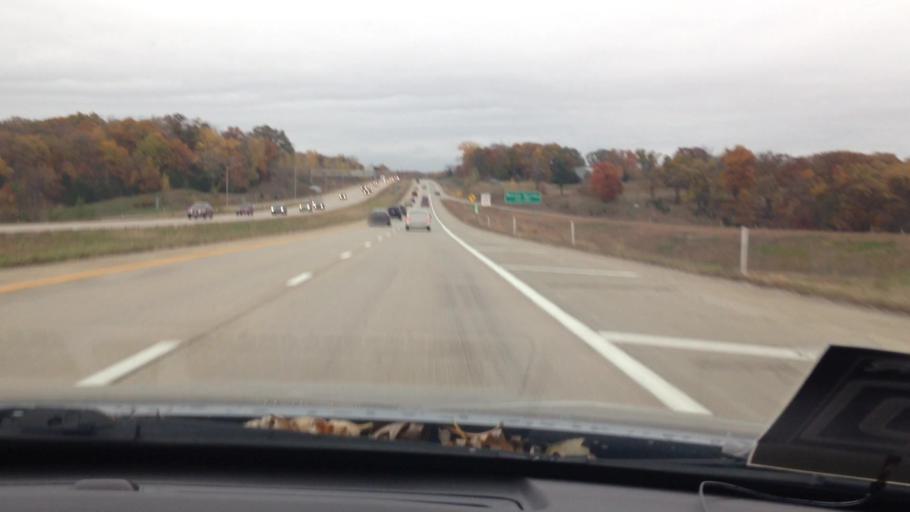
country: US
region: Kansas
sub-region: Leavenworth County
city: Basehor
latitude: 39.1149
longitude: -94.8940
